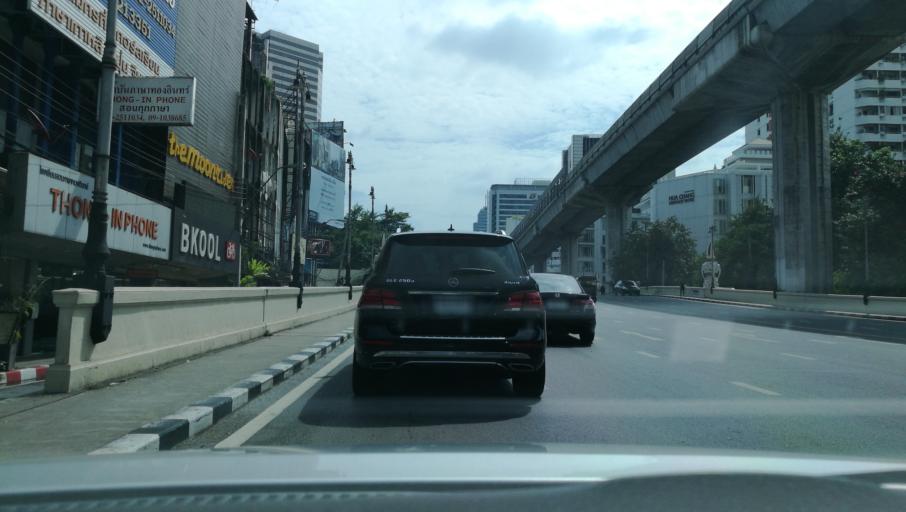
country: TH
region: Bangkok
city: Ratchathewi
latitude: 13.7499
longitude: 100.5315
